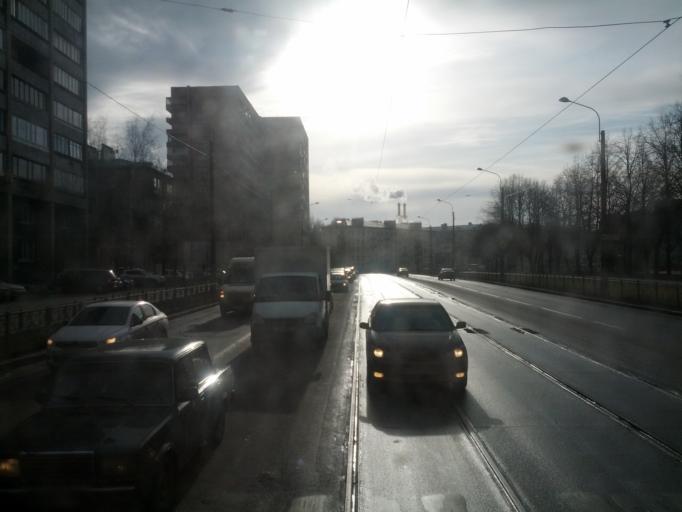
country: RU
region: Leningrad
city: Kalininskiy
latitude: 59.9614
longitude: 30.4131
